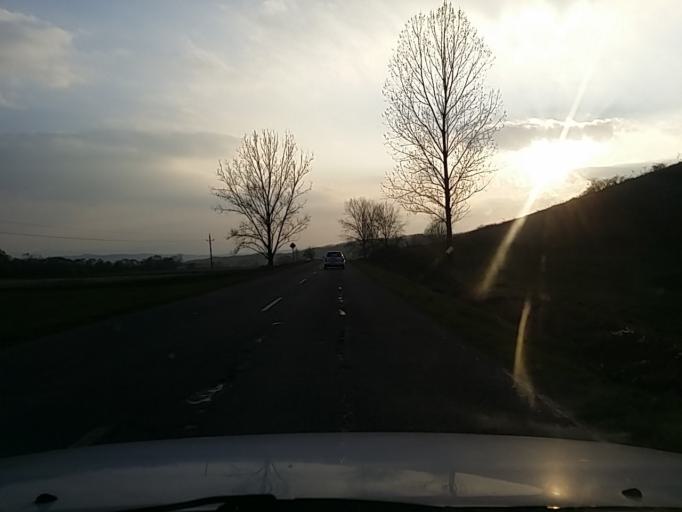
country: HU
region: Heves
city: Tarnalelesz
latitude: 48.0459
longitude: 20.1449
